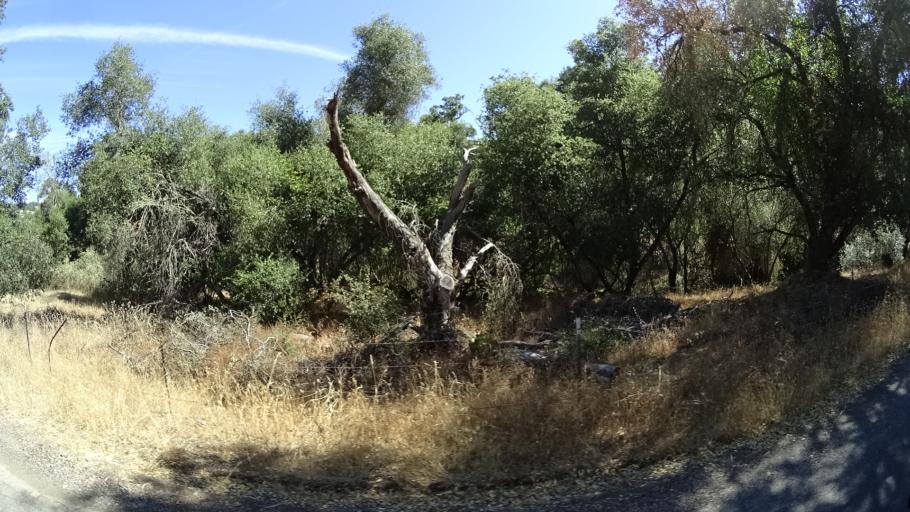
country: US
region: California
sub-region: Calaveras County
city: Angels Camp
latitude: 38.1464
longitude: -120.5702
